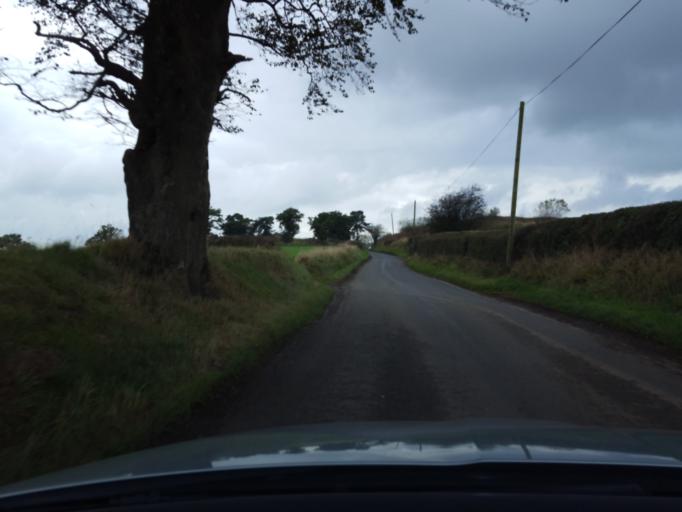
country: GB
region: Scotland
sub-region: West Lothian
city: Bathgate
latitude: 55.9128
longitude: -3.6052
